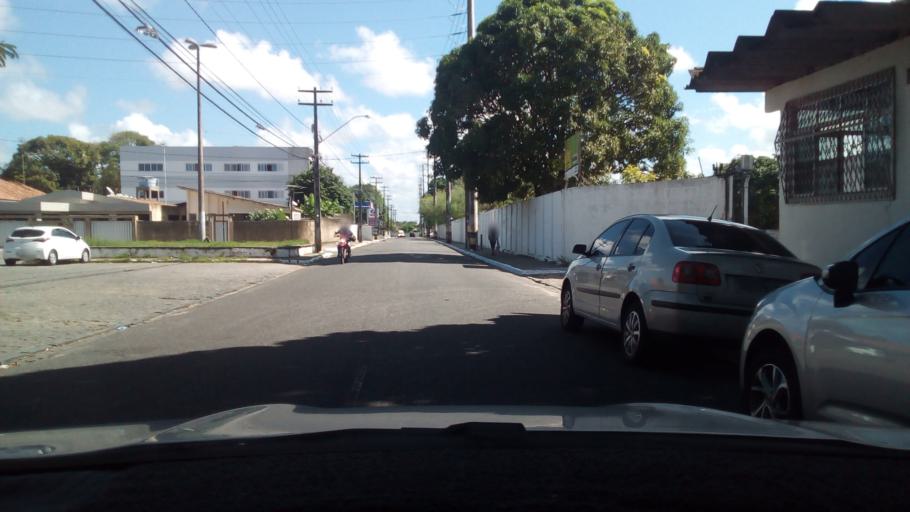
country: BR
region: Paraiba
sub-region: Joao Pessoa
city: Joao Pessoa
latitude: -7.1354
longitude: -34.8721
